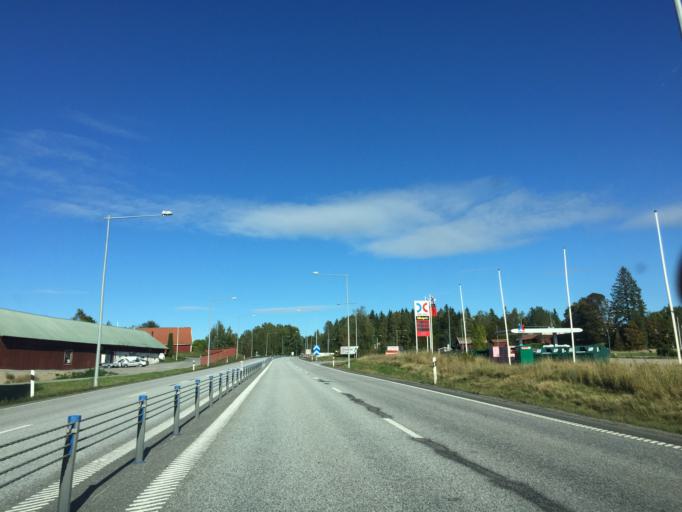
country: SE
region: OErebro
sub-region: Orebro Kommun
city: Hovsta
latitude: 59.3244
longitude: 15.2303
